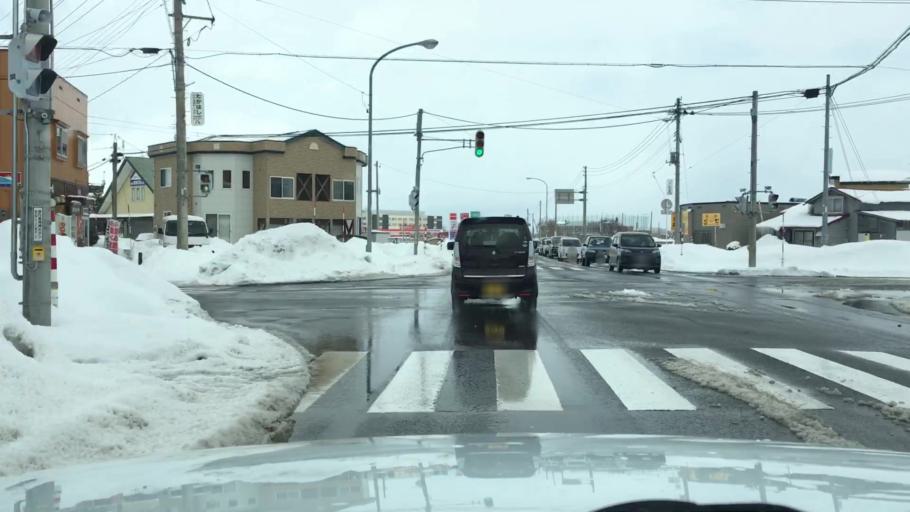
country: JP
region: Aomori
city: Hirosaki
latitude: 40.5819
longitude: 140.4972
